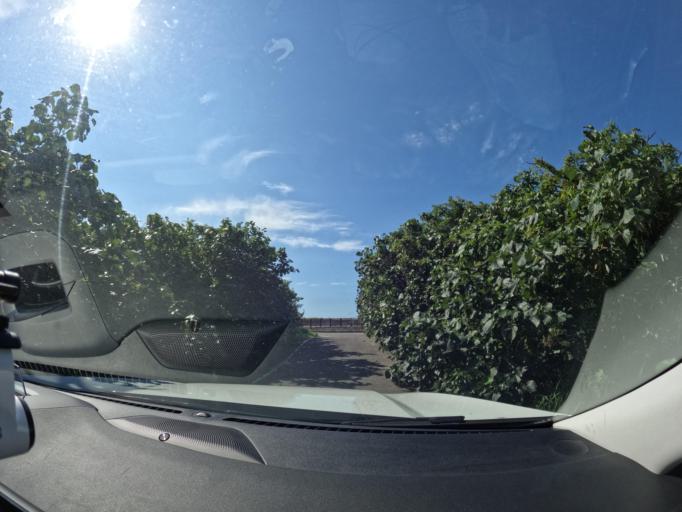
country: TW
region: Taiwan
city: Taoyuan City
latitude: 25.0931
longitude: 121.1895
